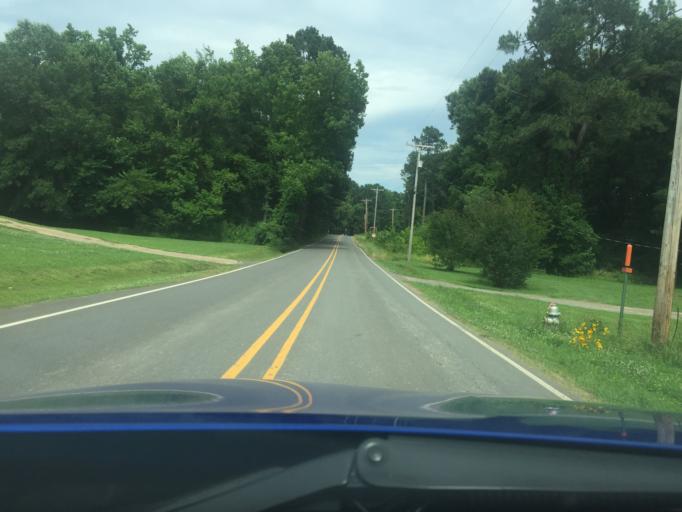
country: US
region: Arkansas
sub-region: Pulaski County
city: Maumelle
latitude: 34.8305
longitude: -92.4428
